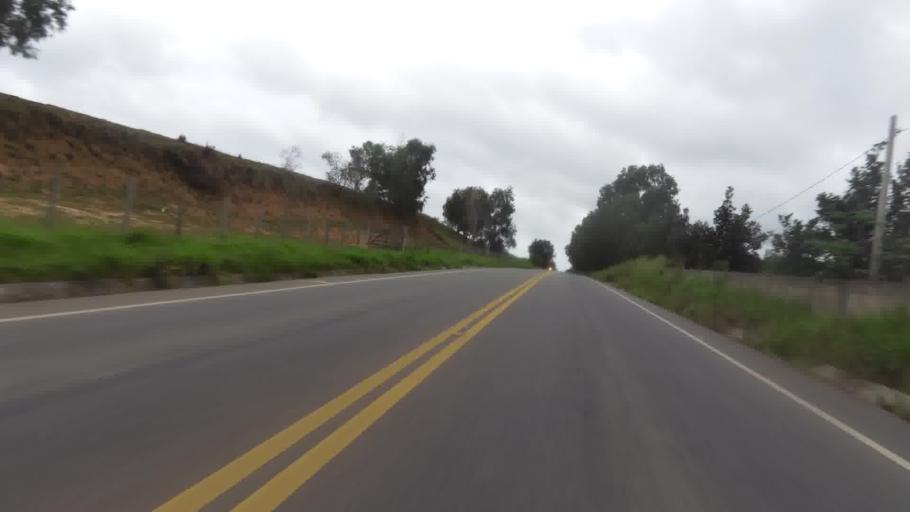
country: BR
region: Espirito Santo
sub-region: Iconha
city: Iconha
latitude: -20.7764
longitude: -40.7589
